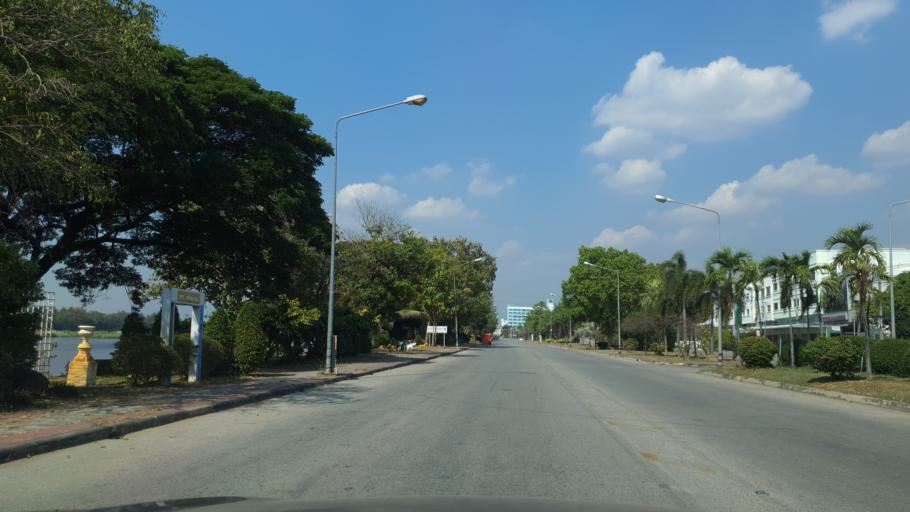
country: TH
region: Tak
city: Tak
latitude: 16.8658
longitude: 99.1243
